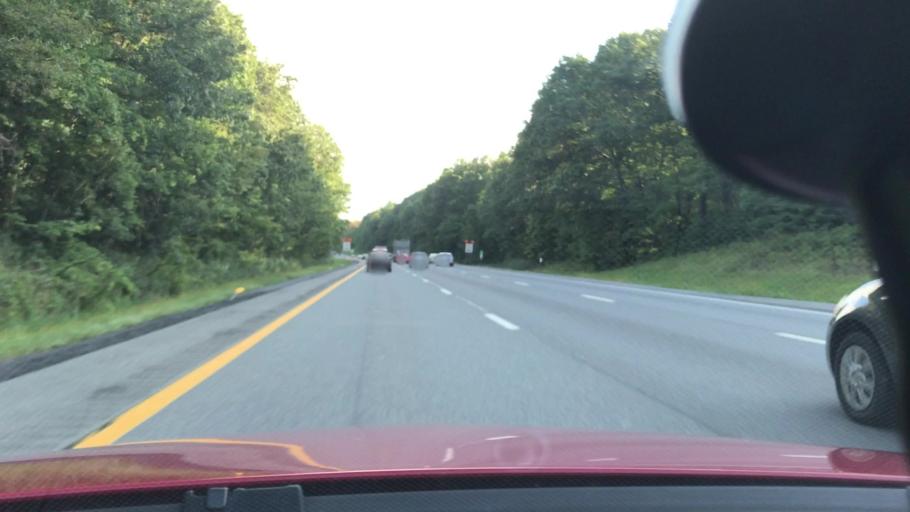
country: US
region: New York
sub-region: Albany County
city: Cohoes
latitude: 42.8128
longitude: -73.7672
